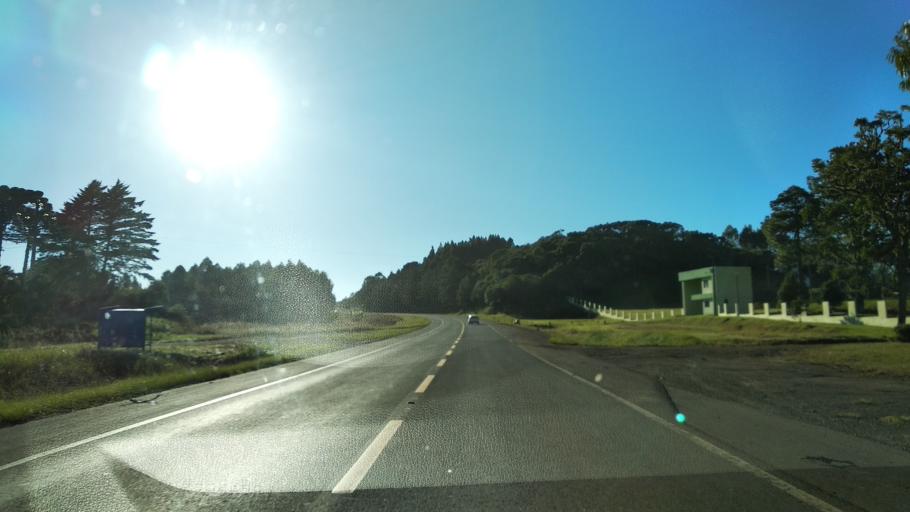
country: BR
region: Santa Catarina
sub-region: Lages
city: Lages
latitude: -27.7953
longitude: -50.3851
